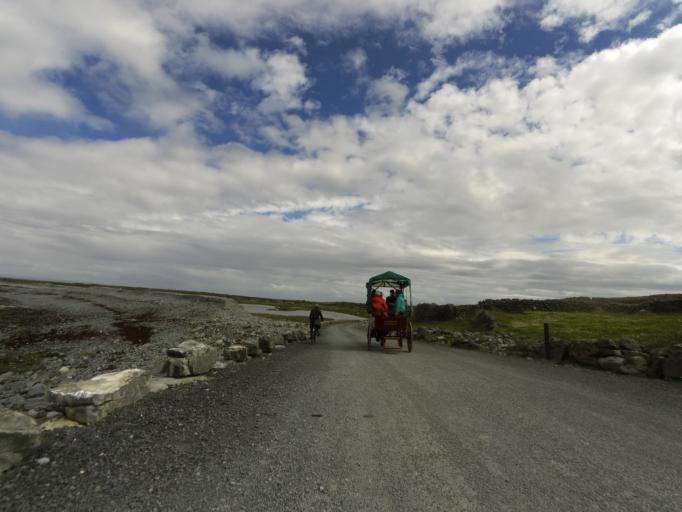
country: IE
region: Connaught
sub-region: County Galway
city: Clifden
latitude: 53.1377
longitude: -9.7118
